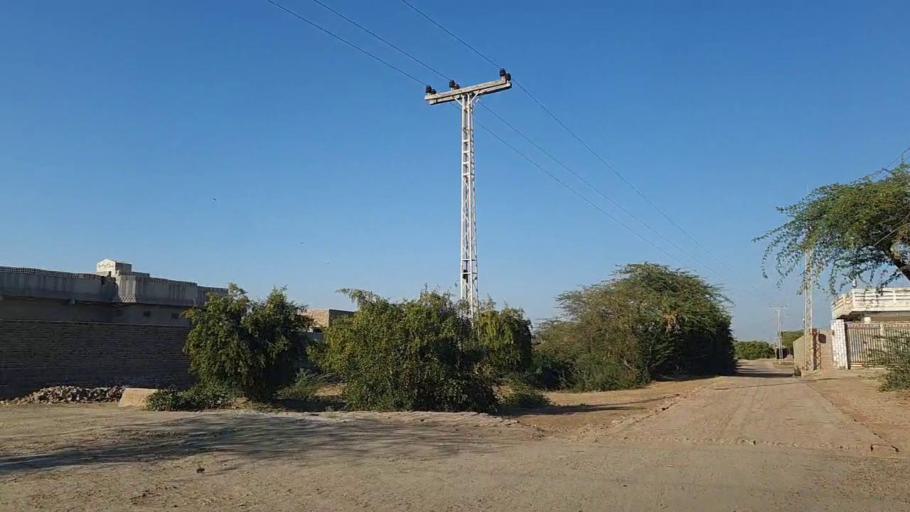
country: PK
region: Sindh
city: Naukot
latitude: 24.9855
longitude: 69.3648
